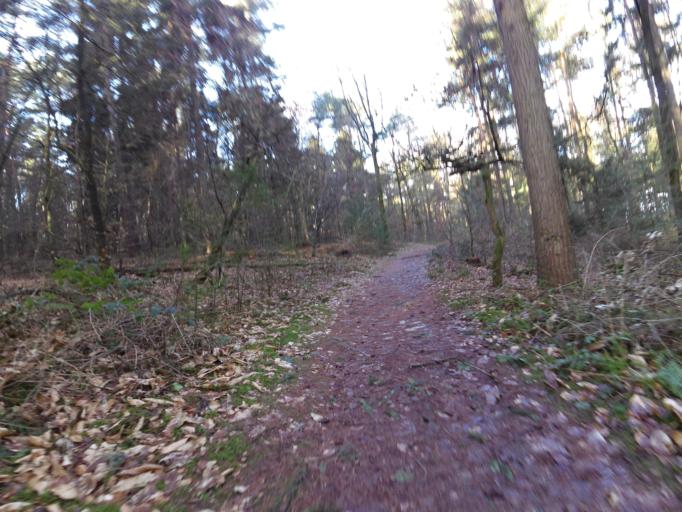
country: NL
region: Gelderland
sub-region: Gemeente Montferland
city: s-Heerenberg
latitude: 51.9250
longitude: 6.2430
